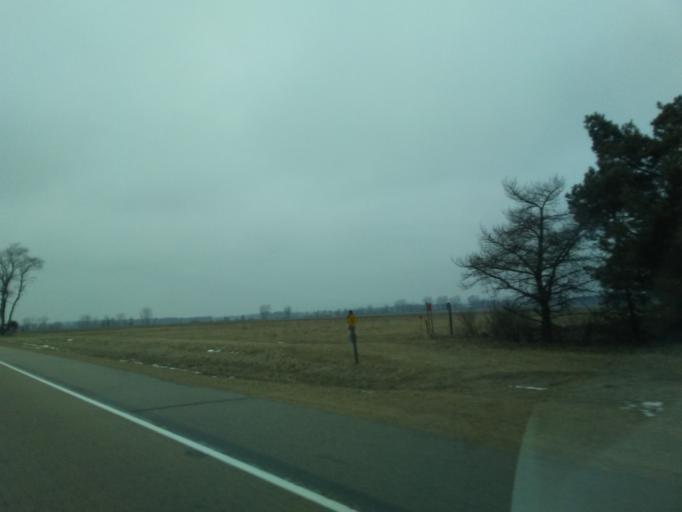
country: US
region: Wisconsin
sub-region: Sauk County
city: Spring Green
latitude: 43.1617
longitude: -89.9653
